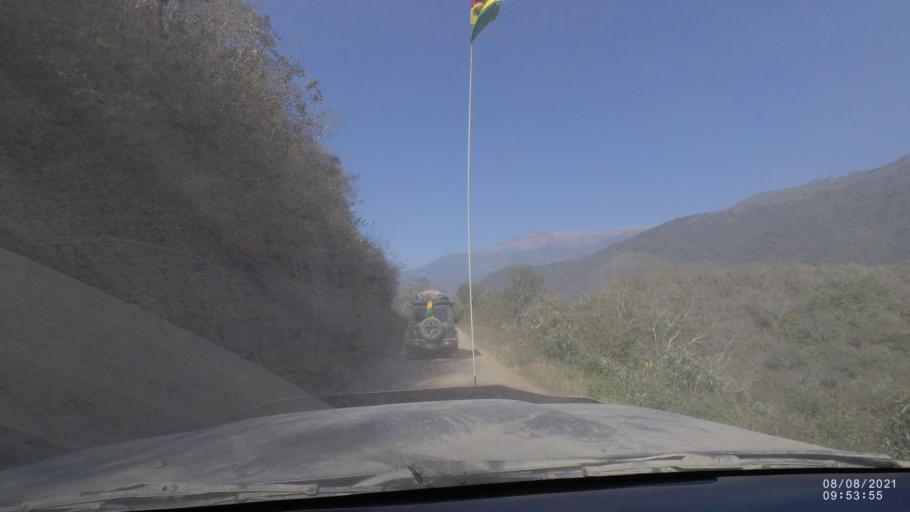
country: BO
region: La Paz
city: Quime
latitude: -16.6309
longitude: -66.7342
